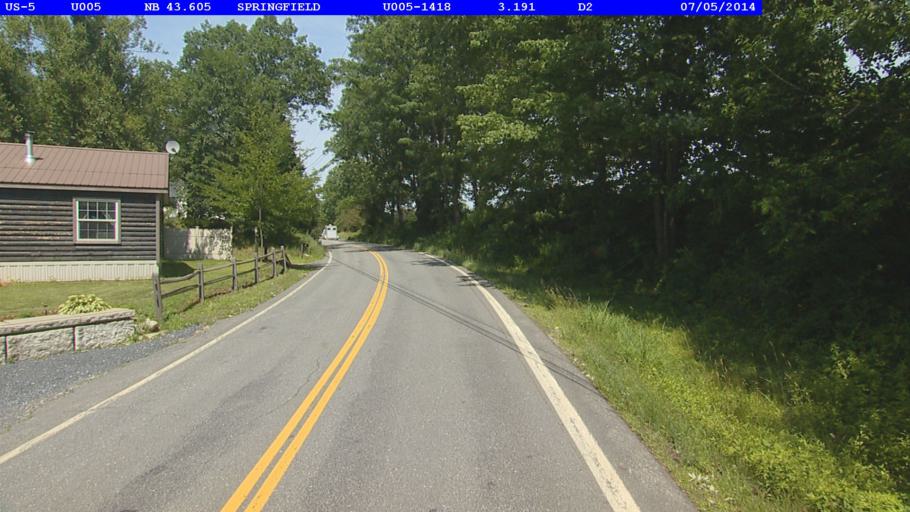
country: US
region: New Hampshire
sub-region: Sullivan County
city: Charlestown
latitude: 43.2624
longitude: -72.4253
